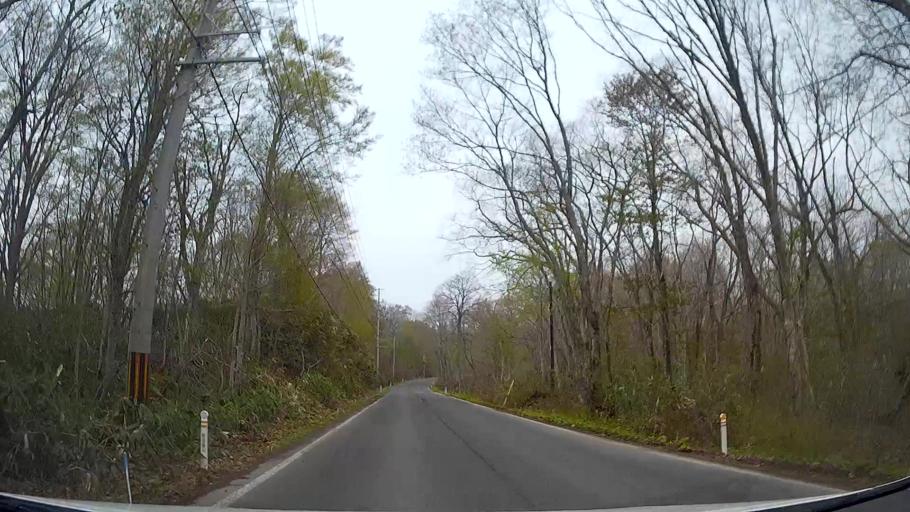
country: JP
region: Akita
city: Hanawa
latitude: 40.3998
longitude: 140.8664
